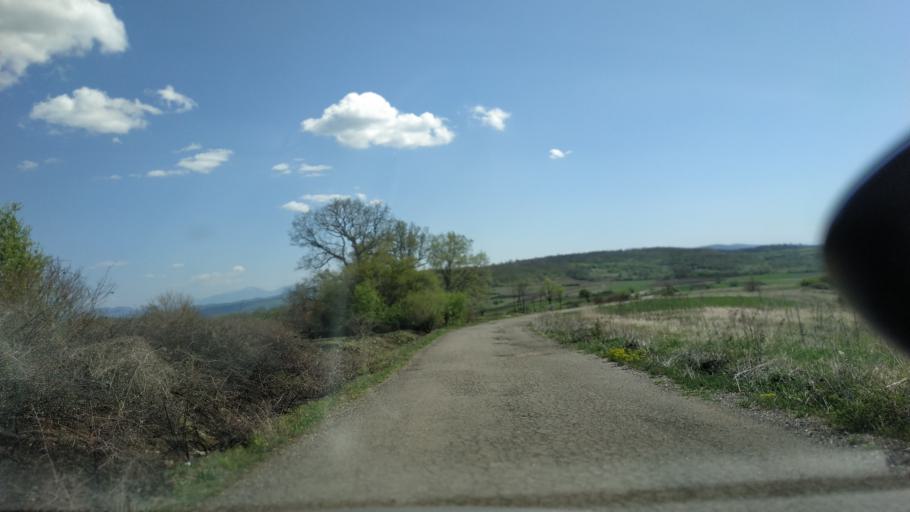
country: RS
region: Central Serbia
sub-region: Zajecarski Okrug
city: Soko Banja
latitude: 43.5203
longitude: 21.9059
